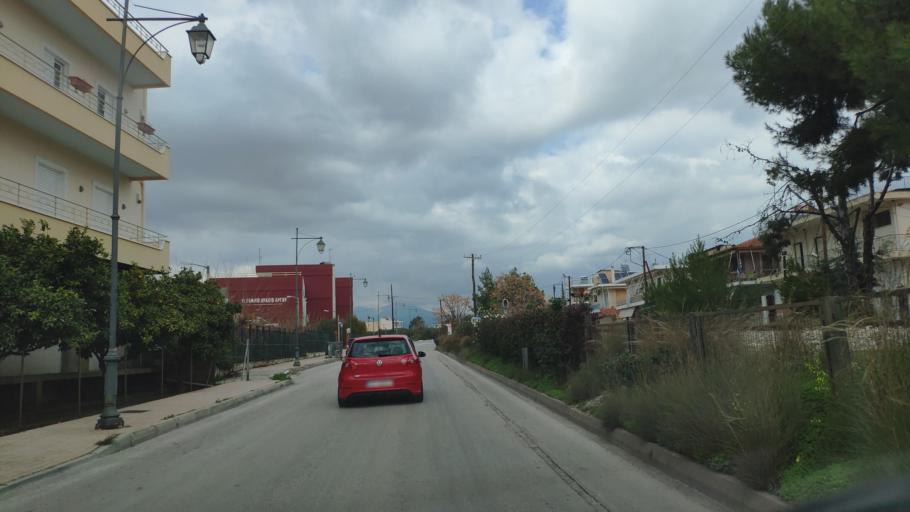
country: GR
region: Peloponnese
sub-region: Nomos Argolidos
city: Argos
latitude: 37.6419
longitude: 22.7320
